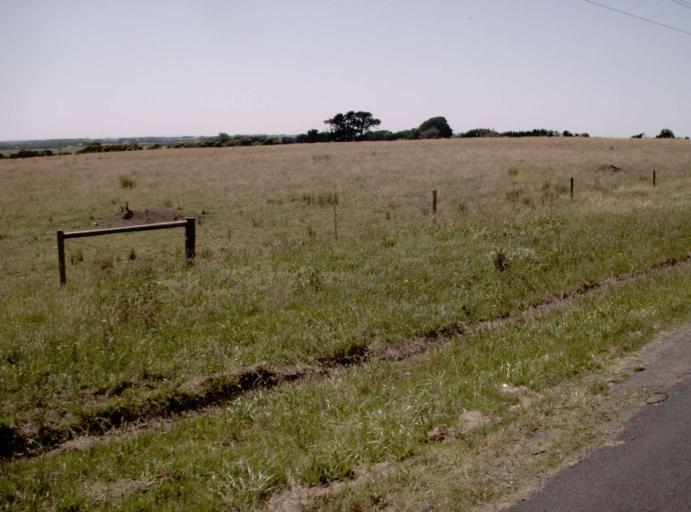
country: AU
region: Victoria
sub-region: Bass Coast
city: North Wonthaggi
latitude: -38.6184
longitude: 145.6006
